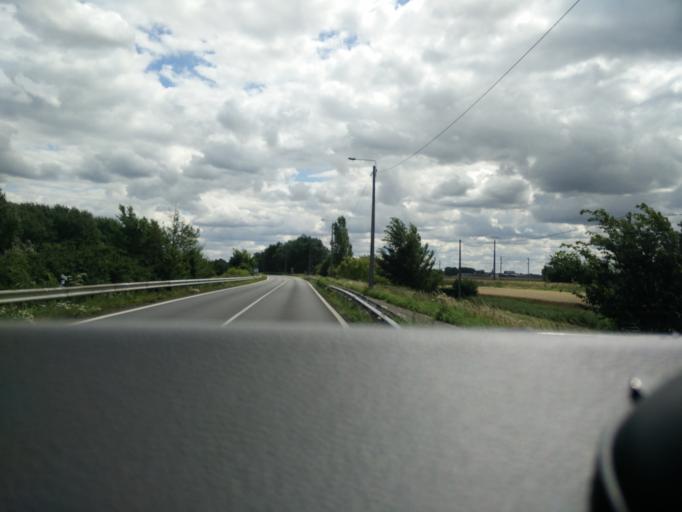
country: FR
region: Nord-Pas-de-Calais
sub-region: Departement du Nord
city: Coudekerque-Village
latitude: 50.9863
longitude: 2.4043
